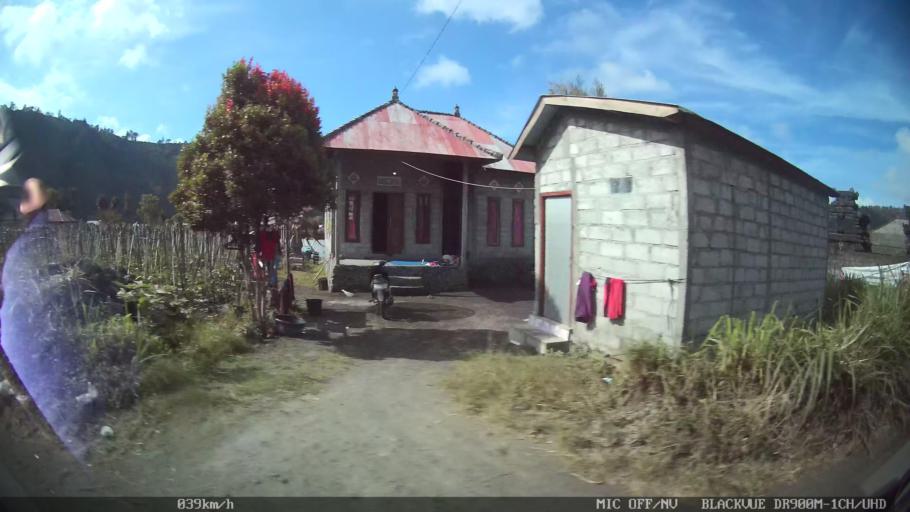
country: ID
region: Bali
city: Banjar Trunyan
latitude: -8.2161
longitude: 115.3811
